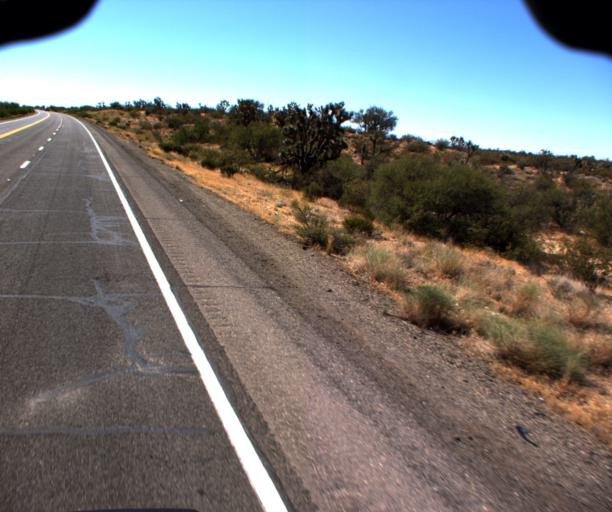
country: US
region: Arizona
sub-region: Yavapai County
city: Congress
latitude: 34.1947
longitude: -113.0571
